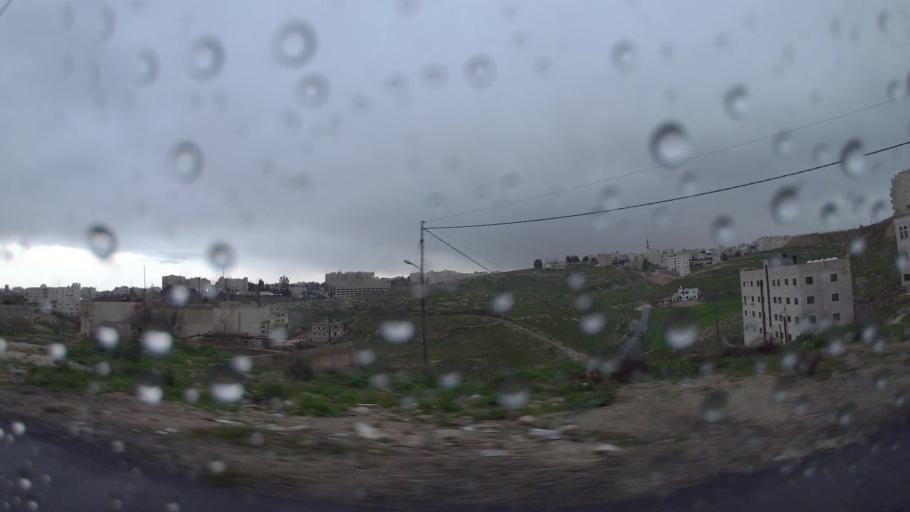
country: JO
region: Amman
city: Amman
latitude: 31.9985
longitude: 35.9672
